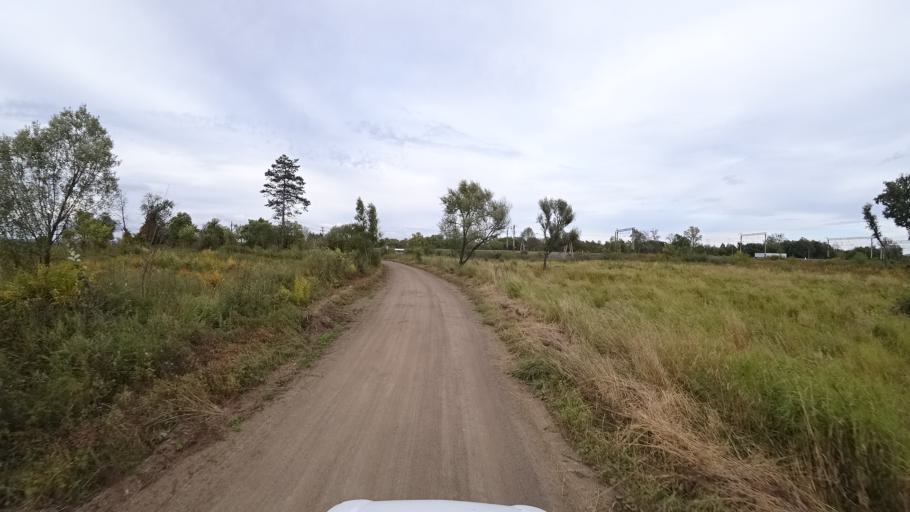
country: RU
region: Amur
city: Arkhara
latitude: 49.3520
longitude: 130.1555
